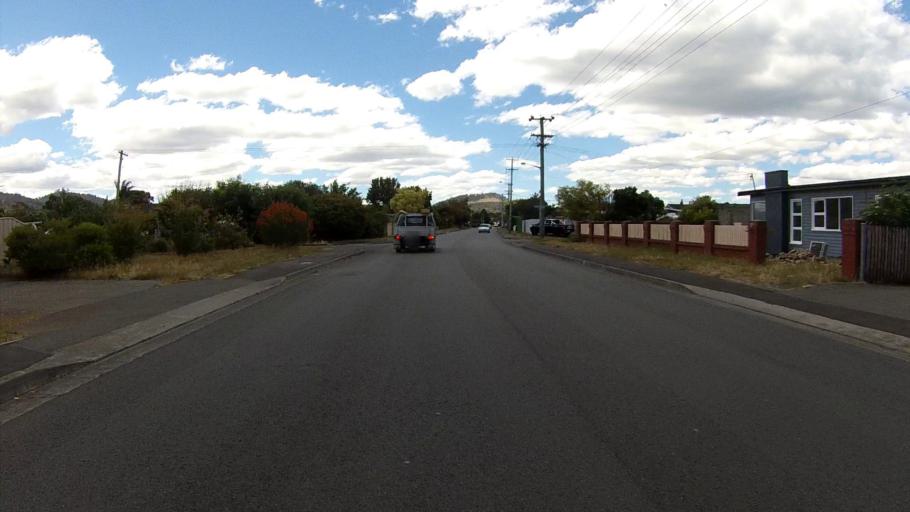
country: AU
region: Tasmania
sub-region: Clarence
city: Lauderdale
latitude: -42.9066
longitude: 147.4926
